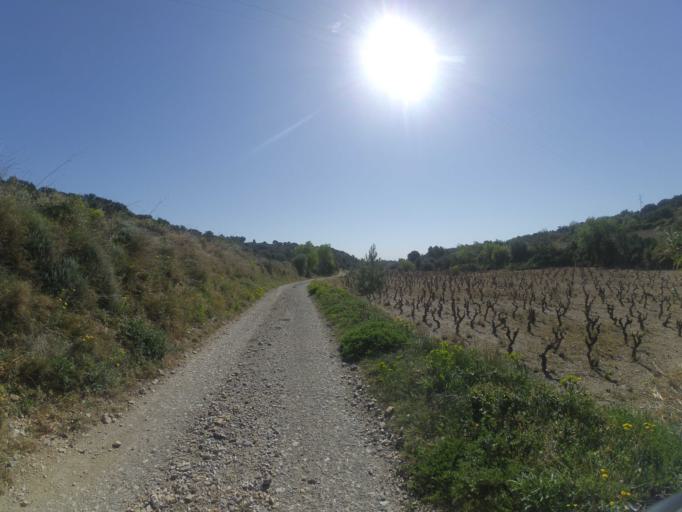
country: FR
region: Languedoc-Roussillon
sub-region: Departement des Pyrenees-Orientales
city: Baixas
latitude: 42.7597
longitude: 2.7874
